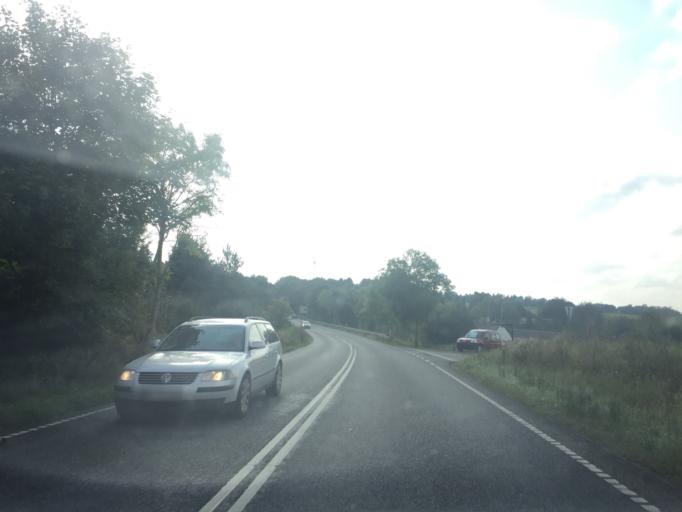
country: DK
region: Zealand
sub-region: Lejre Kommune
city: Ejby
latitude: 55.6535
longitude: 11.8122
